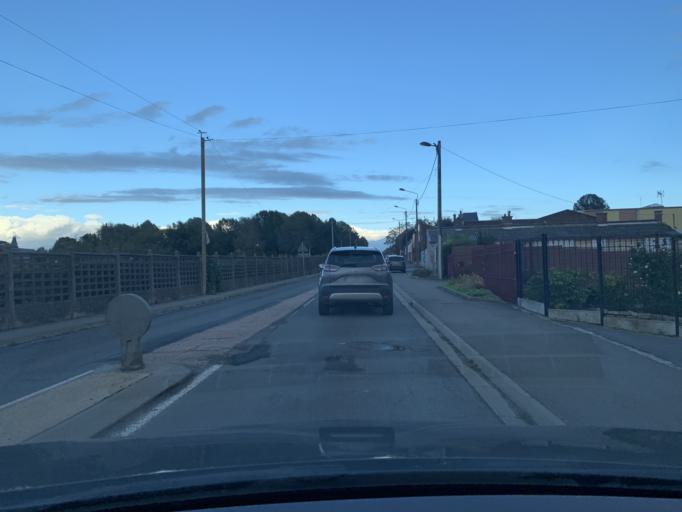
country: FR
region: Nord-Pas-de-Calais
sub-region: Departement du Nord
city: Cambrai
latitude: 50.1676
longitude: 3.2264
